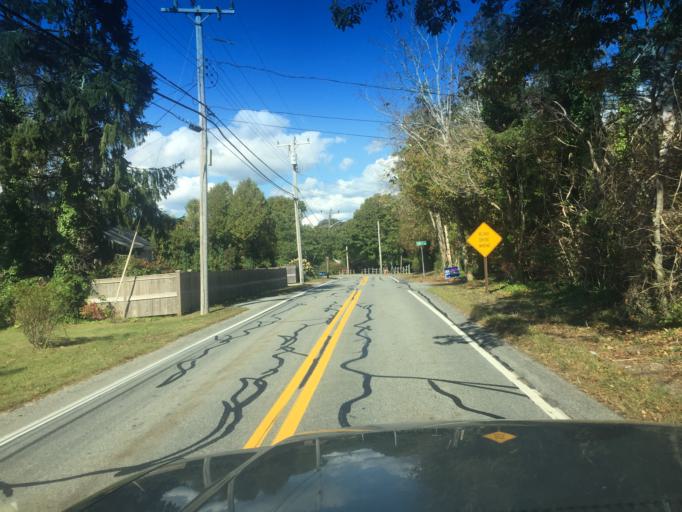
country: US
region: Massachusetts
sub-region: Barnstable County
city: Pocasset
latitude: 41.6693
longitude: -70.6074
